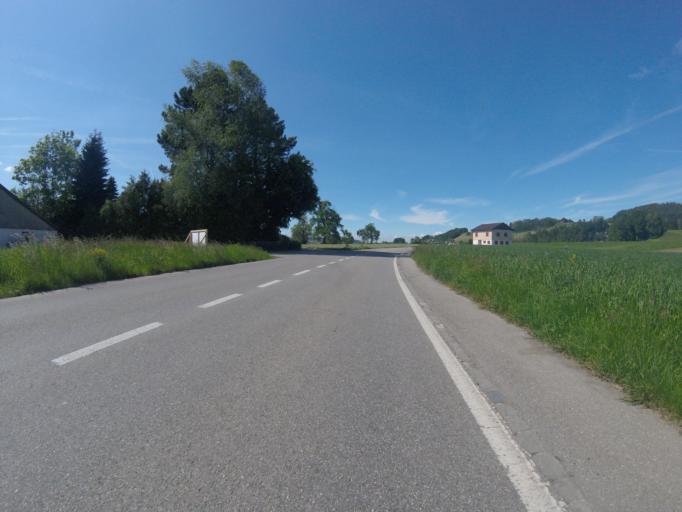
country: CH
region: Saint Gallen
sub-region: Wahlkreis Toggenburg
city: Ganterschwil
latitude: 47.3856
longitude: 9.0855
